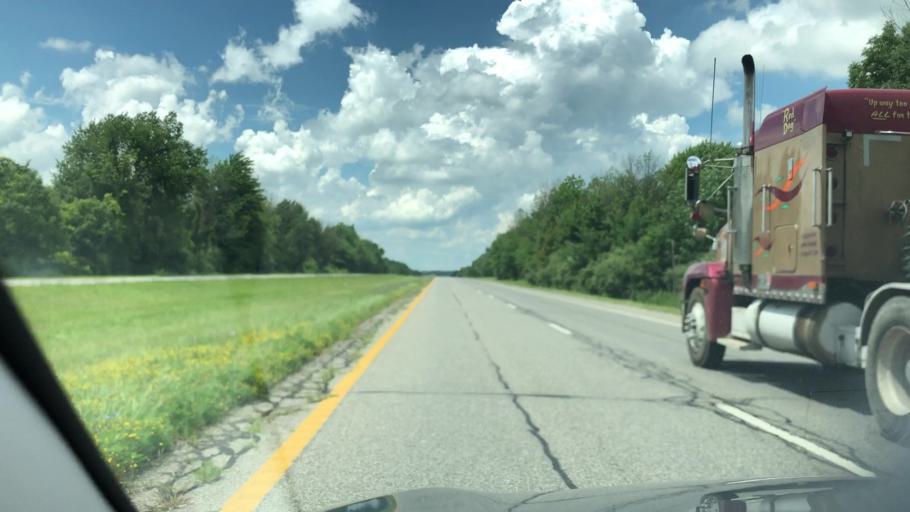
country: US
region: Ohio
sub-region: Stark County
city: Canal Fulton
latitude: 40.8933
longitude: -81.6270
